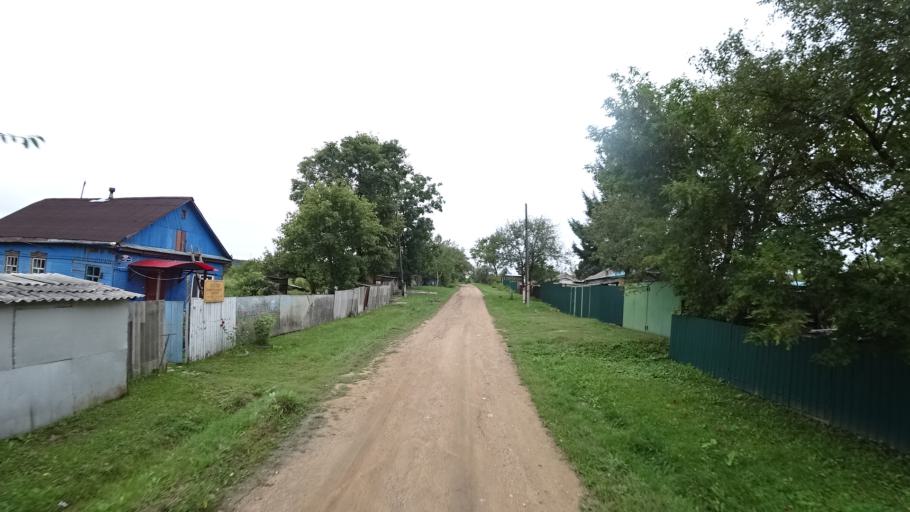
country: RU
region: Primorskiy
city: Rettikhovka
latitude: 44.1690
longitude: 132.7678
